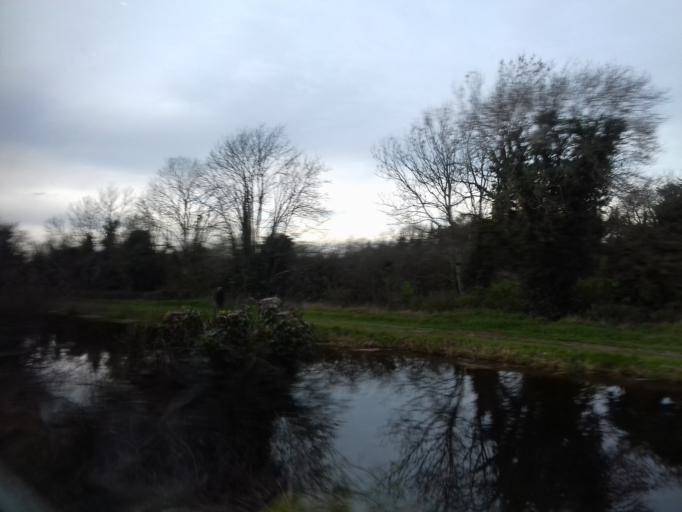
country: IE
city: Confey
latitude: 53.3733
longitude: -6.4753
